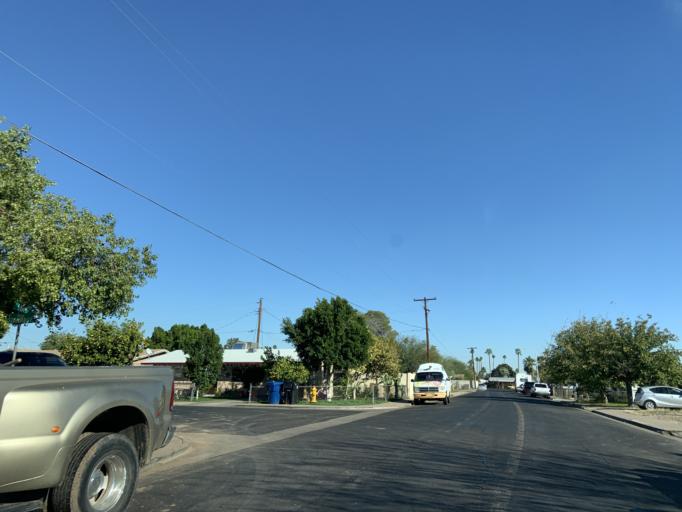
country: US
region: Arizona
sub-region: Maricopa County
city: Mesa
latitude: 33.4044
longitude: -111.8614
